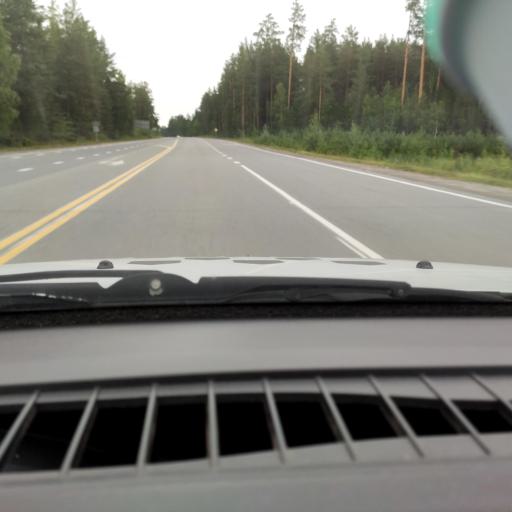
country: RU
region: Chelyabinsk
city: Kyshtym
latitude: 55.6942
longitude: 60.5012
